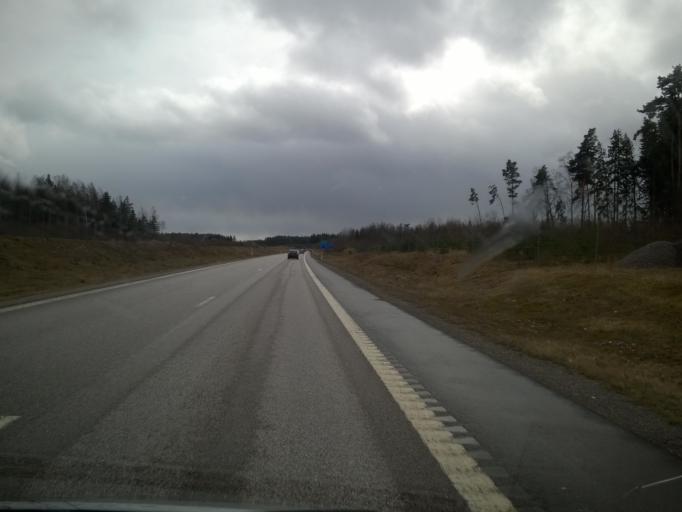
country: SE
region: Uppsala
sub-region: Osthammars Kommun
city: Bjorklinge
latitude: 60.0288
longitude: 17.6275
